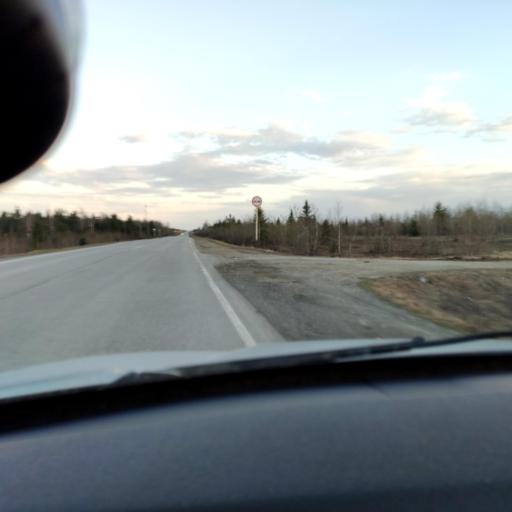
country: RU
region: Perm
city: Gremyachinsk
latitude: 58.5812
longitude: 57.7707
